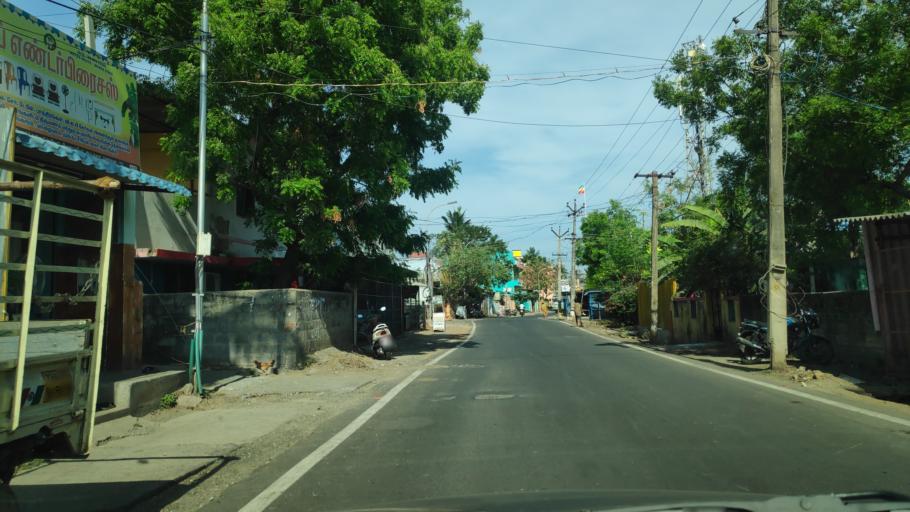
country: IN
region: Tamil Nadu
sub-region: Thiruvallur
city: Ambattur
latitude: 13.1223
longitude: 80.1624
